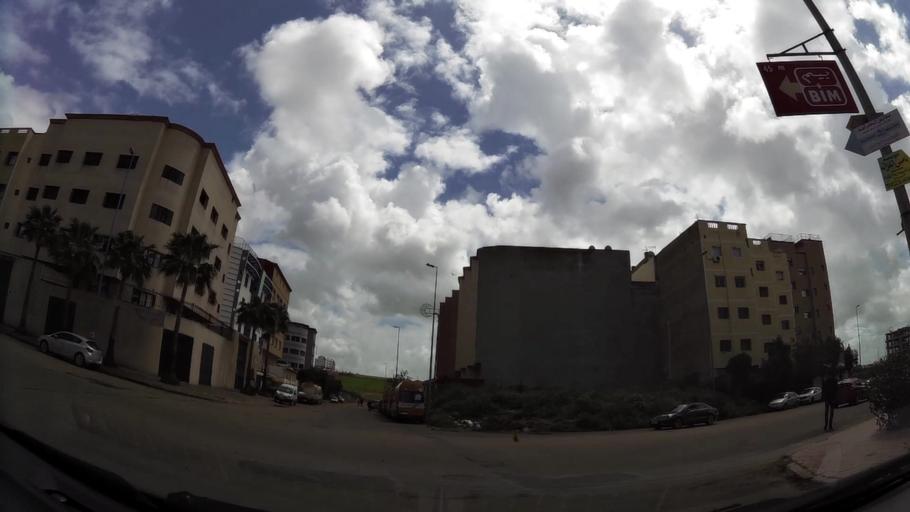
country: MA
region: Grand Casablanca
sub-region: Casablanca
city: Casablanca
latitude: 33.5298
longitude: -7.6022
